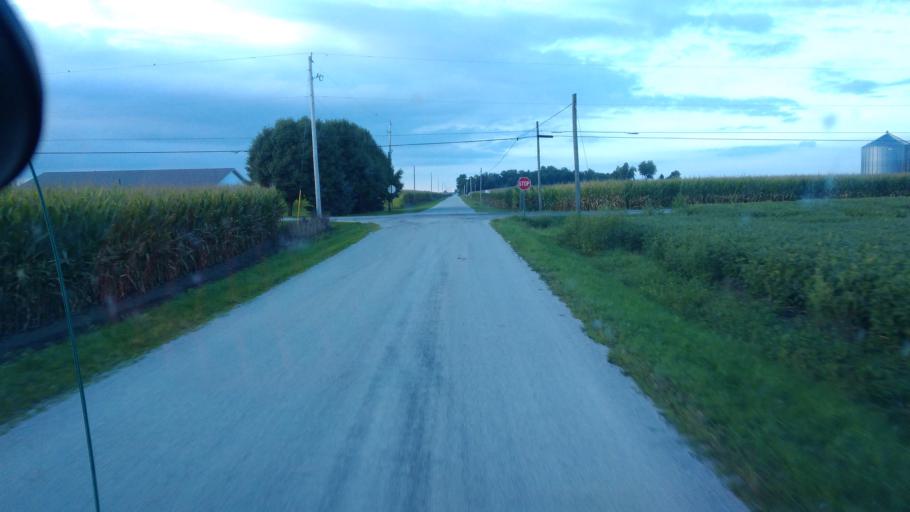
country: US
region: Ohio
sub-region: Hardin County
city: Kenton
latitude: 40.6573
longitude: -83.5148
